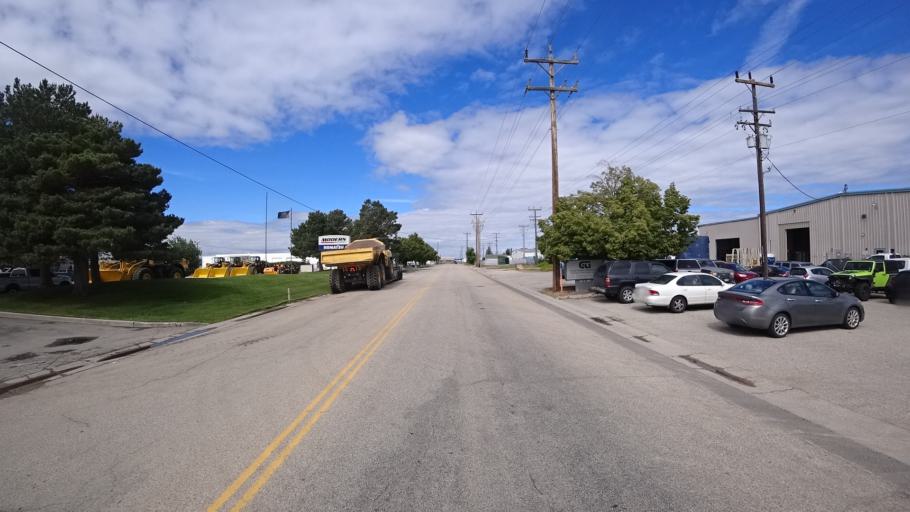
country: US
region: Idaho
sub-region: Ada County
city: Boise
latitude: 43.5604
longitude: -116.1962
